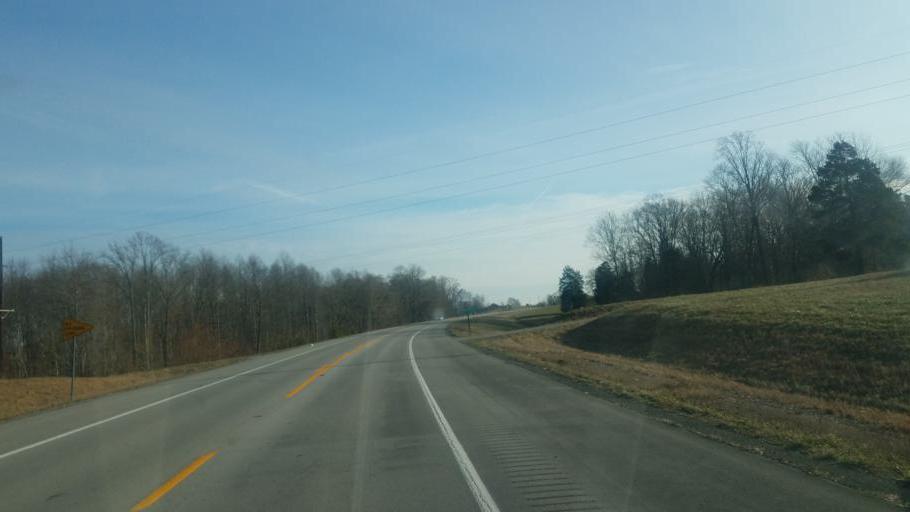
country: US
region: Kentucky
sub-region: Russell County
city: Jamestown
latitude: 36.9971
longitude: -85.0785
